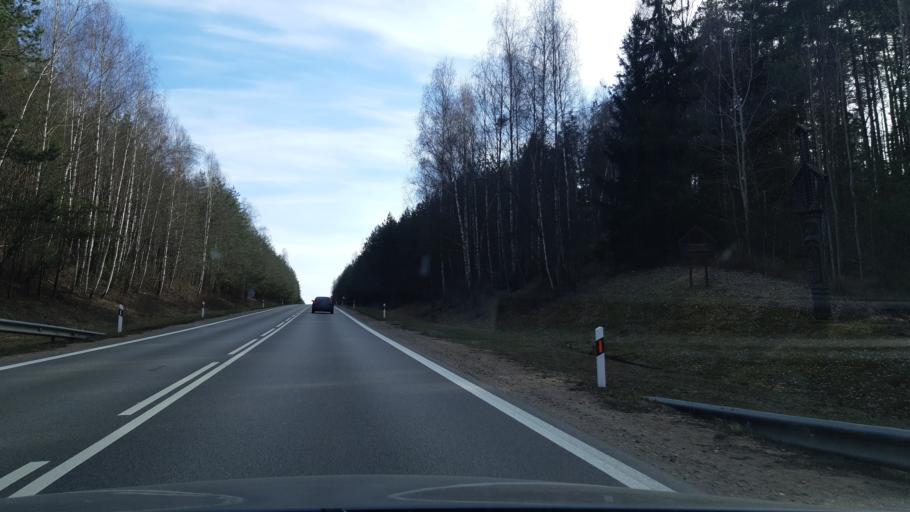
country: LT
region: Alytaus apskritis
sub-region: Alytaus rajonas
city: Daugai
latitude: 54.1422
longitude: 24.2106
